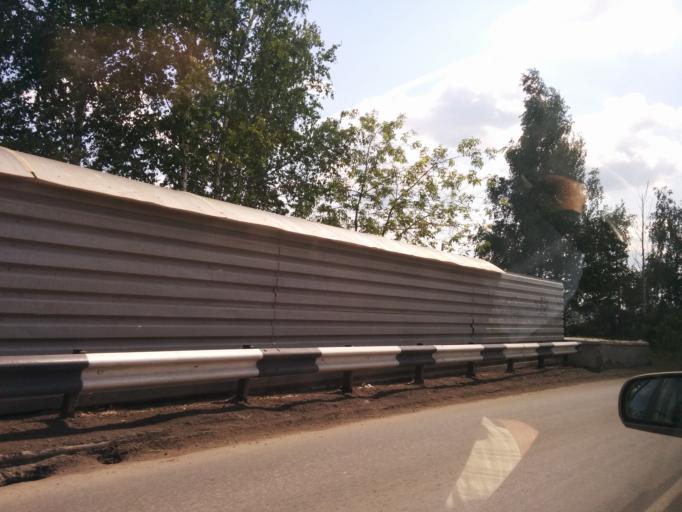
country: RU
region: Perm
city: Perm
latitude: 58.1145
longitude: 56.3228
